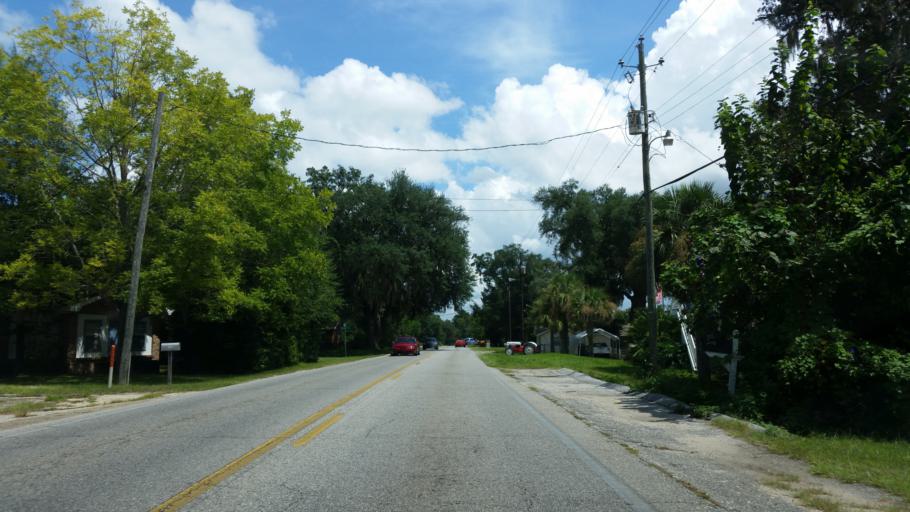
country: US
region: Florida
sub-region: Santa Rosa County
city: Milton
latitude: 30.6346
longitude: -87.0355
